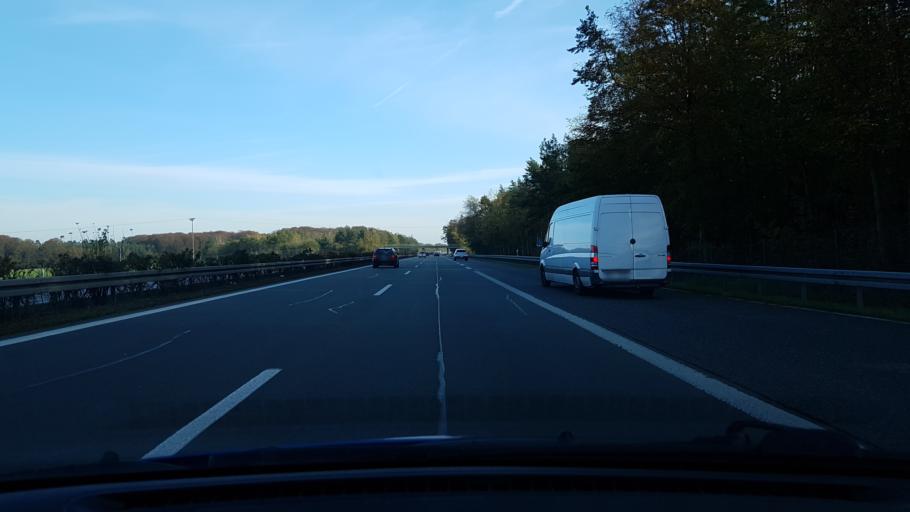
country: DE
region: Mecklenburg-Vorpommern
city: Wittenburg
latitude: 53.4951
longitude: 11.1295
